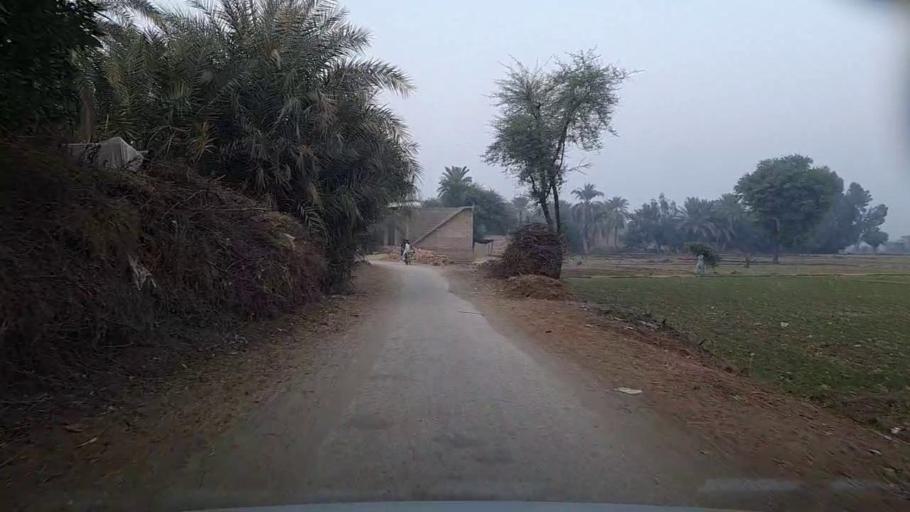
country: PK
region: Sindh
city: Bozdar
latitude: 27.0672
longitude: 68.5973
